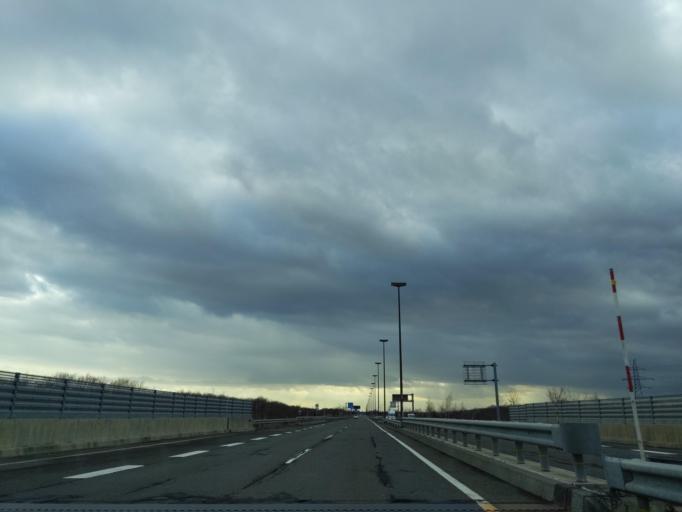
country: JP
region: Hokkaido
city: Chitose
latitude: 42.8251
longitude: 141.6876
